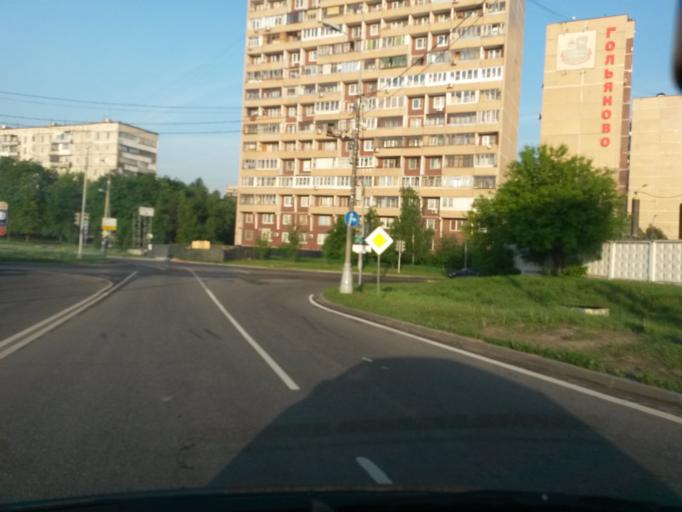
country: RU
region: Moscow
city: Gol'yanovo
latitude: 55.8296
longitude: 37.8253
